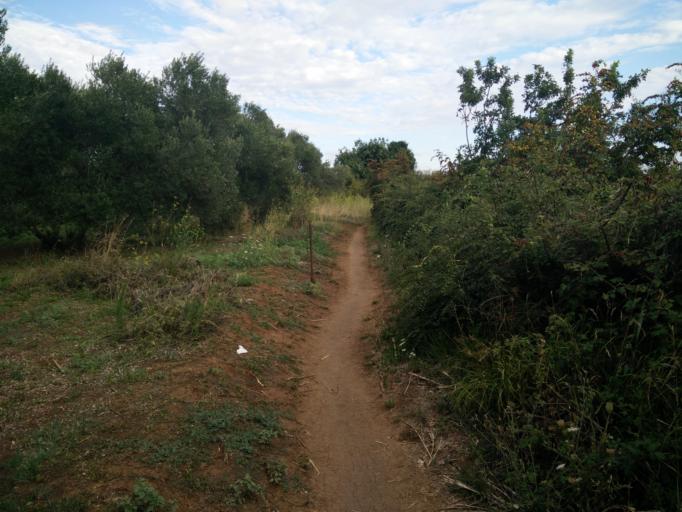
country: HR
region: Zadarska
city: Biograd na Moru
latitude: 43.9519
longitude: 15.4394
